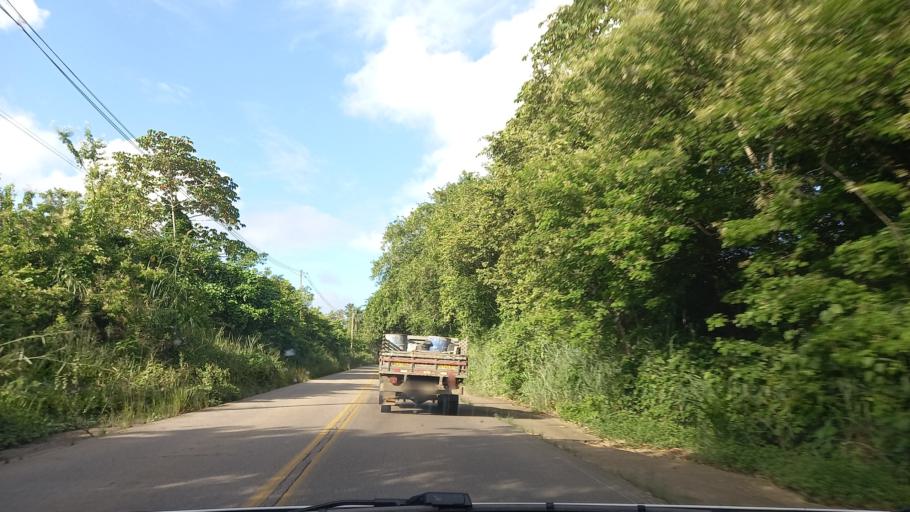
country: BR
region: Pernambuco
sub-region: Rio Formoso
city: Rio Formoso
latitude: -8.6576
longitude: -35.1423
